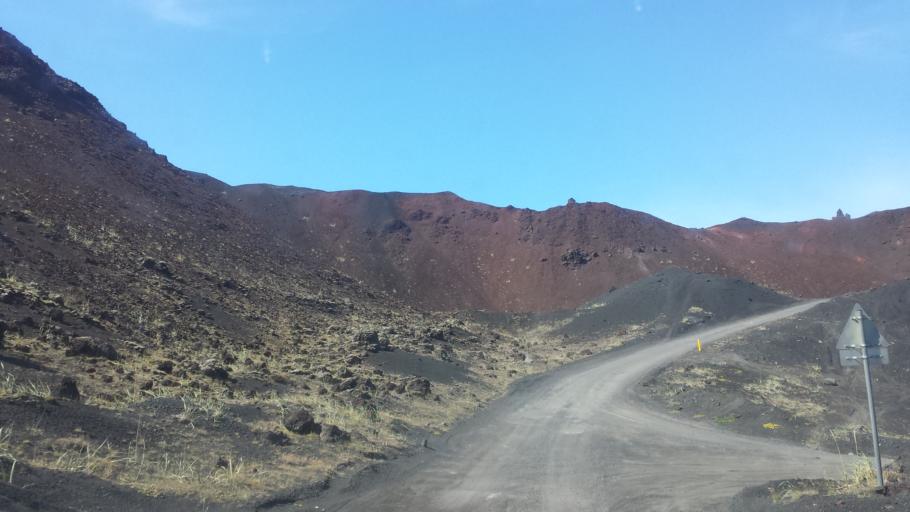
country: IS
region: South
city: Vestmannaeyjar
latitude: 63.4403
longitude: -20.2357
